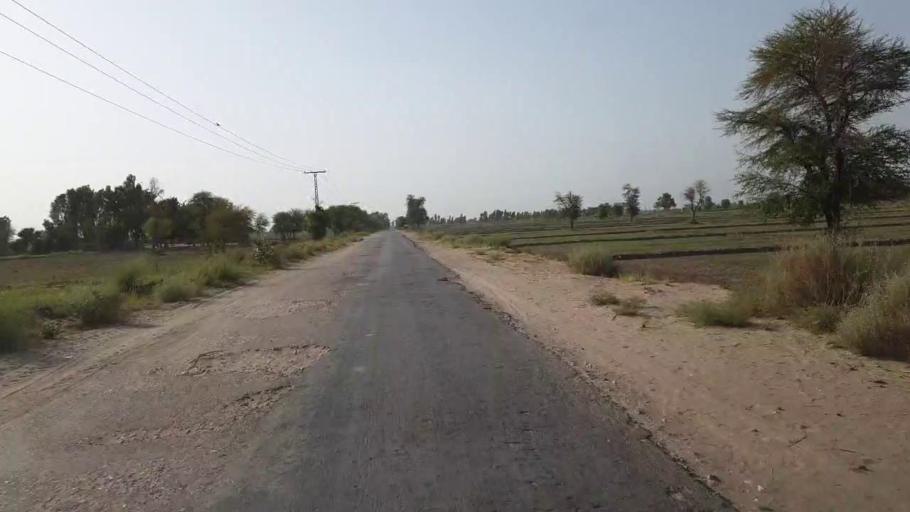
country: PK
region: Sindh
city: Jam Sahib
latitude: 26.3852
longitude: 68.8837
